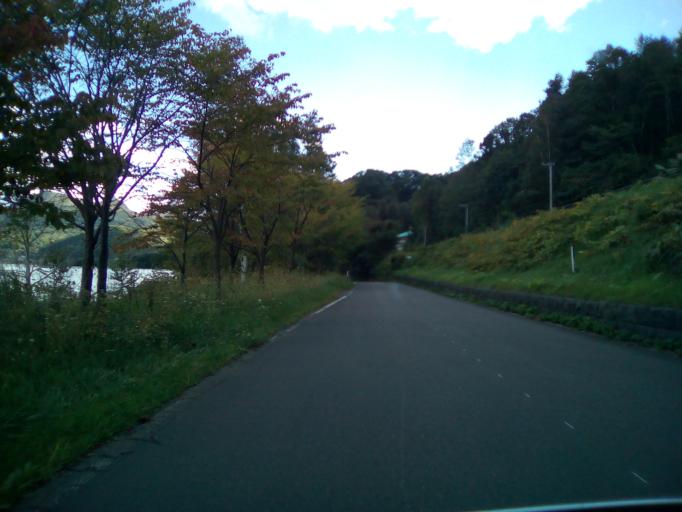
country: JP
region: Hokkaido
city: Date
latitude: 42.5818
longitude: 140.7957
